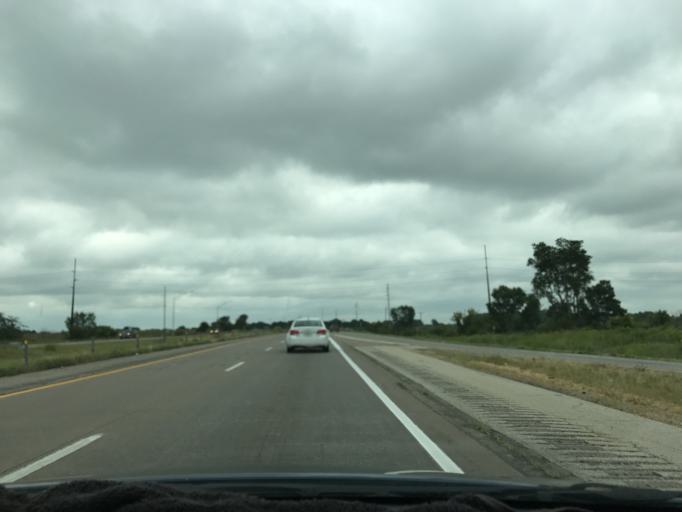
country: US
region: Iowa
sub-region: Scott County
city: Eldridge
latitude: 41.5953
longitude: -90.5653
